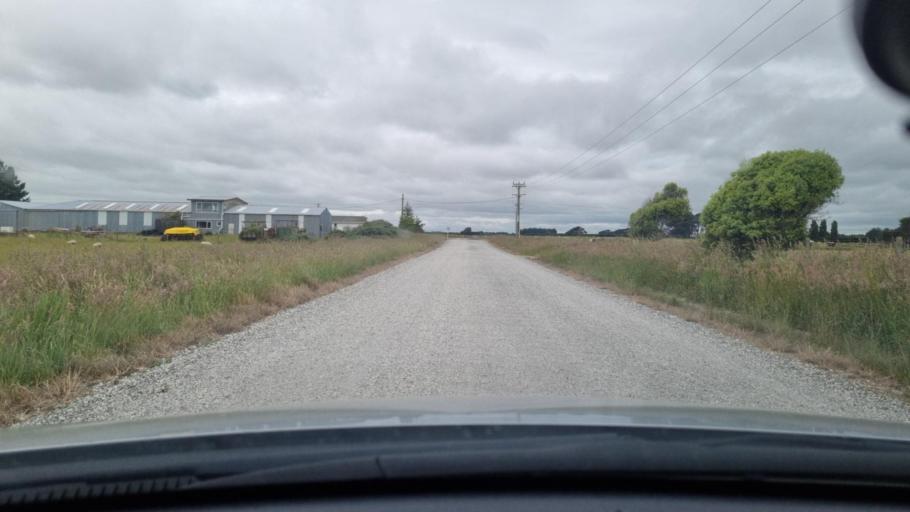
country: NZ
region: Southland
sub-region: Invercargill City
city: Invercargill
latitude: -46.3710
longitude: 168.2985
